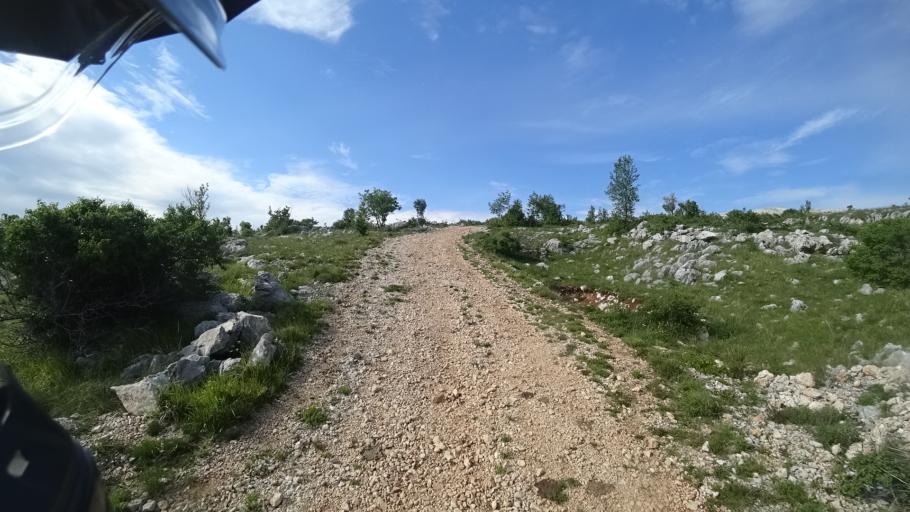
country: HR
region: Splitsko-Dalmatinska
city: Hrvace
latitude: 43.7843
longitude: 16.4372
